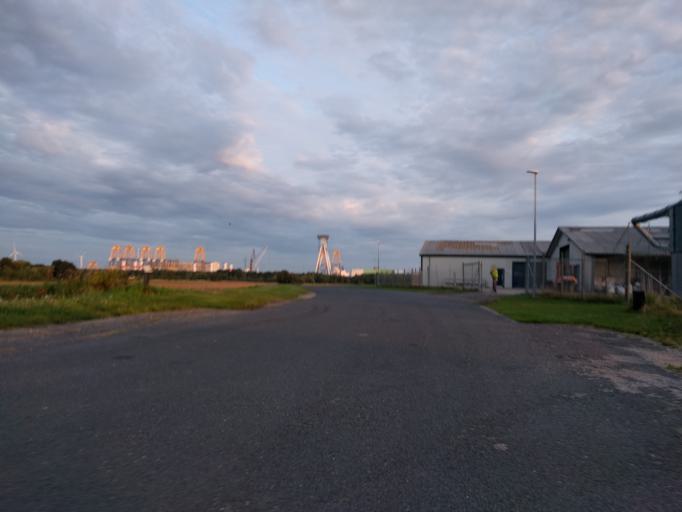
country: DK
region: South Denmark
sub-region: Kerteminde Kommune
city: Munkebo
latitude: 55.4604
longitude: 10.5442
